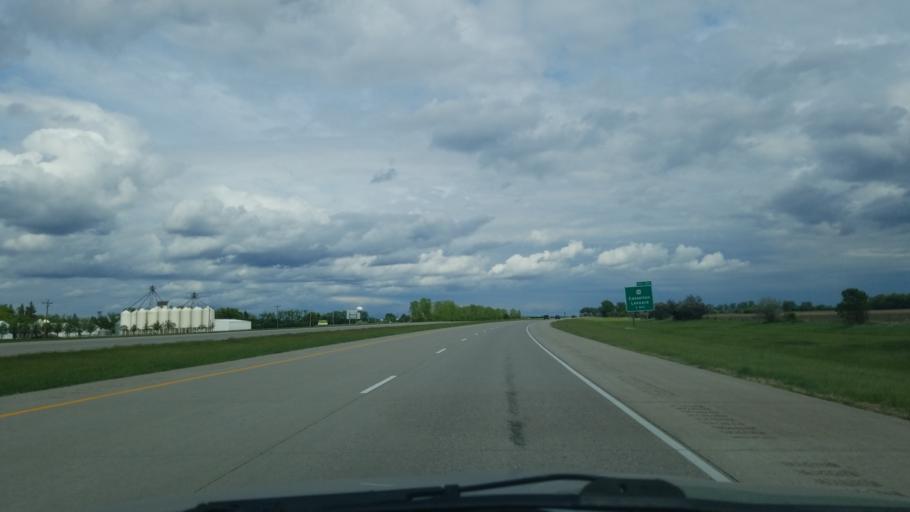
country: US
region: North Dakota
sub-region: Cass County
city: Casselton
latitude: 46.8758
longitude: -97.2390
